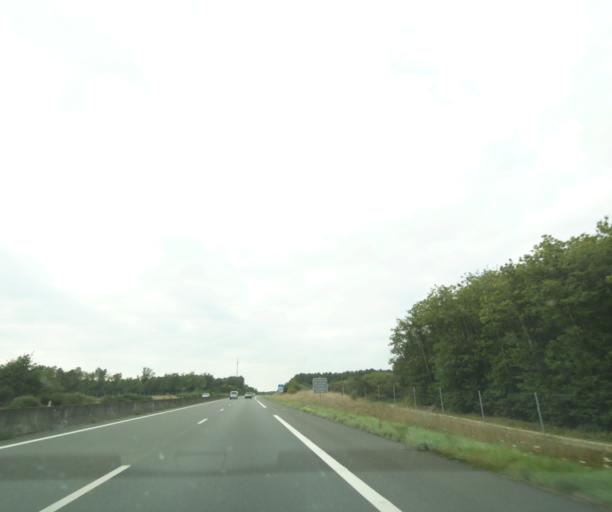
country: FR
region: Pays de la Loire
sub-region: Departement de la Sarthe
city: Luceau
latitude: 47.7019
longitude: 0.3532
